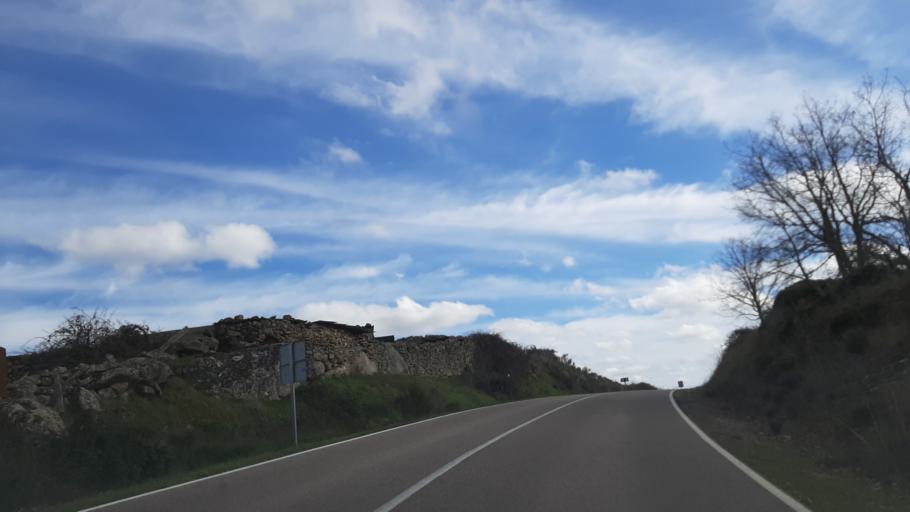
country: ES
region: Castille and Leon
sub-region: Provincia de Salamanca
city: Villarino de los Aires
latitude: 41.2630
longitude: -6.4266
